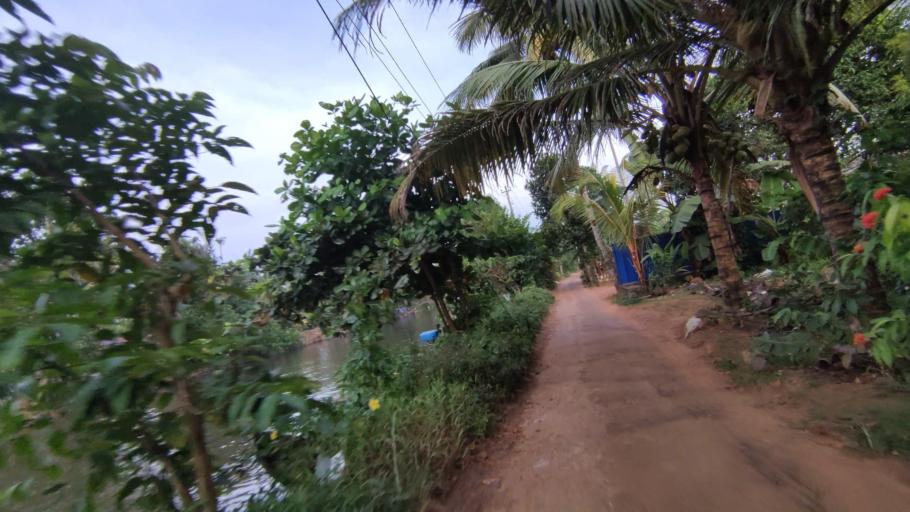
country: IN
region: Kerala
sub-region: Kottayam
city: Kottayam
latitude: 9.6481
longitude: 76.4790
